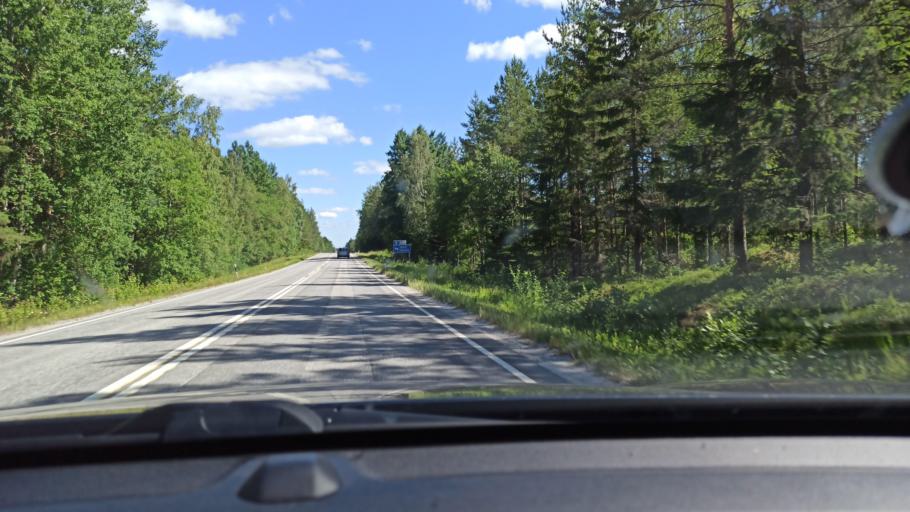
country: FI
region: Ostrobothnia
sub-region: Vaasa
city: Malax
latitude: 62.9835
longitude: 21.6259
